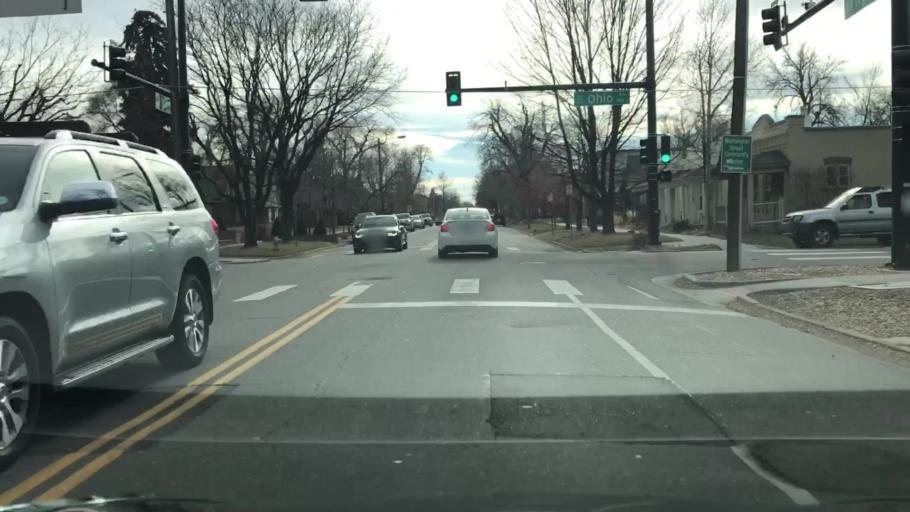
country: US
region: Colorado
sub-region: Denver County
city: Denver
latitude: 39.7022
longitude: -104.9828
